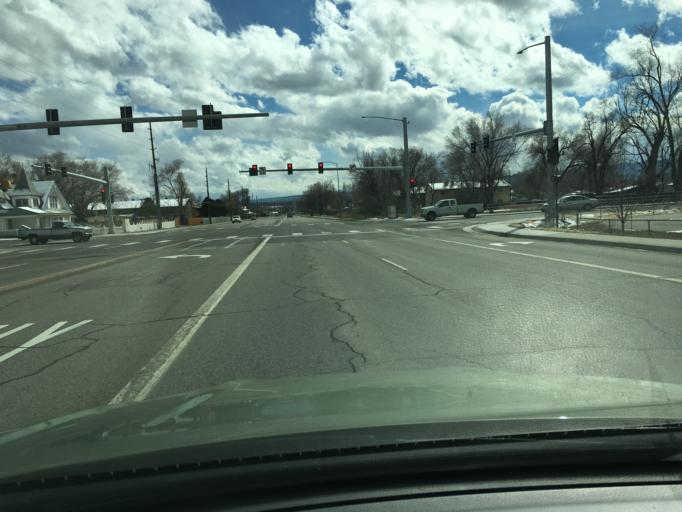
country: US
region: Colorado
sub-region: Mesa County
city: Clifton
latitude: 39.0778
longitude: -108.4595
